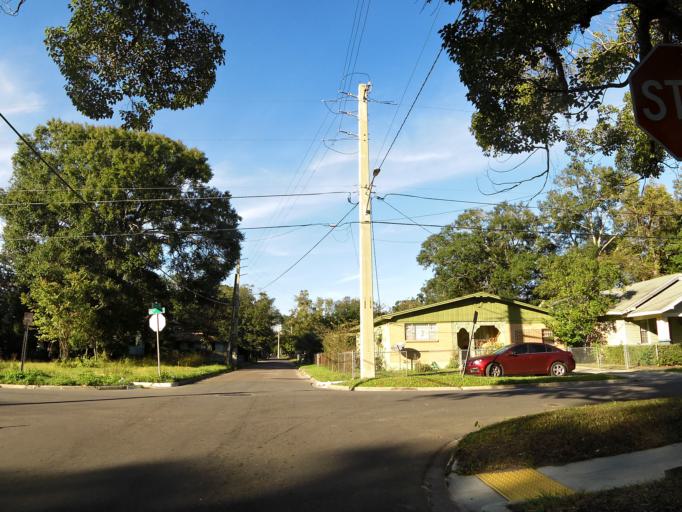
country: US
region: Florida
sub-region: Duval County
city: Jacksonville
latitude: 30.3440
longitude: -81.6798
